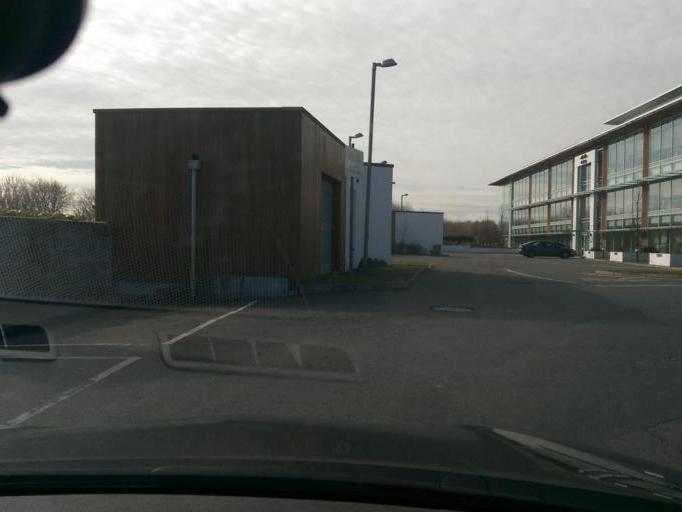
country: IE
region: Connaught
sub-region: County Galway
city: Oranmore
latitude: 53.2772
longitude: -8.9314
